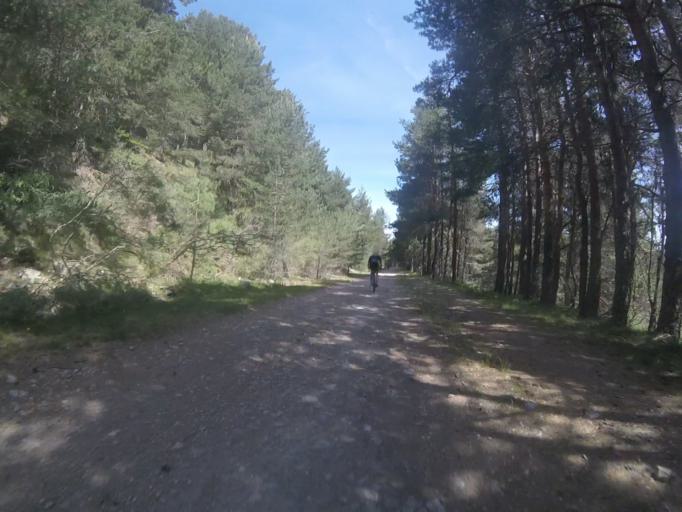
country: ES
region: Madrid
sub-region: Provincia de Madrid
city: Cercedilla
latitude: 40.8077
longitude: -4.0554
